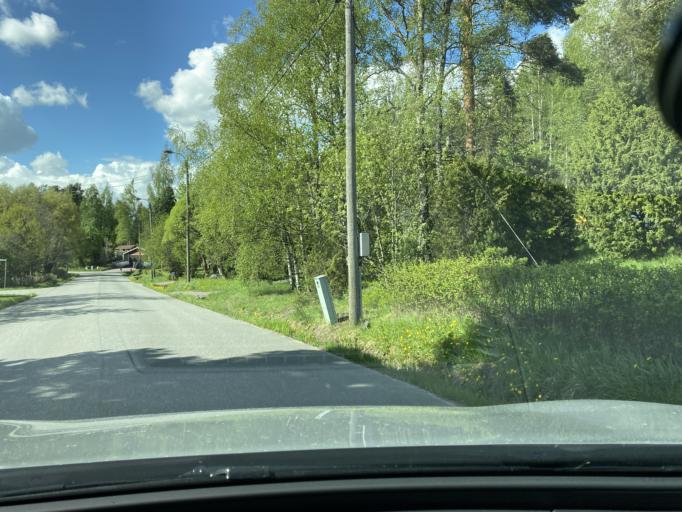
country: FI
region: Uusimaa
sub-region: Helsinki
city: Maentsaelae
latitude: 60.6470
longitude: 25.3232
